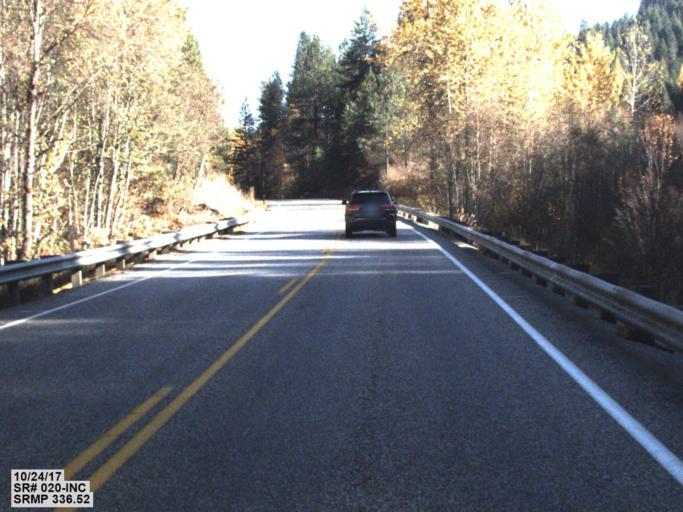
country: US
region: Washington
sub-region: Stevens County
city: Kettle Falls
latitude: 48.5865
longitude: -118.1961
